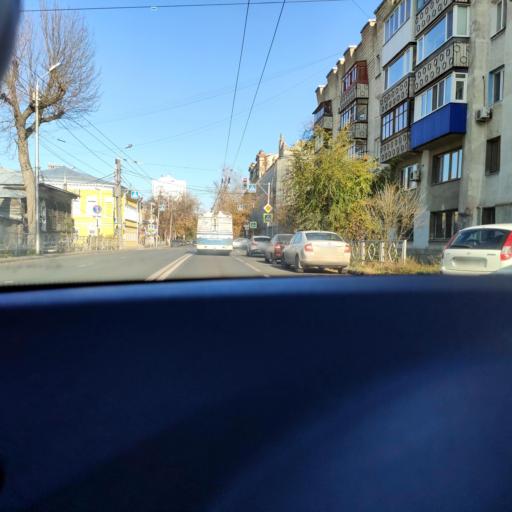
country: RU
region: Samara
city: Rozhdestveno
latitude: 53.1814
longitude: 50.0799
